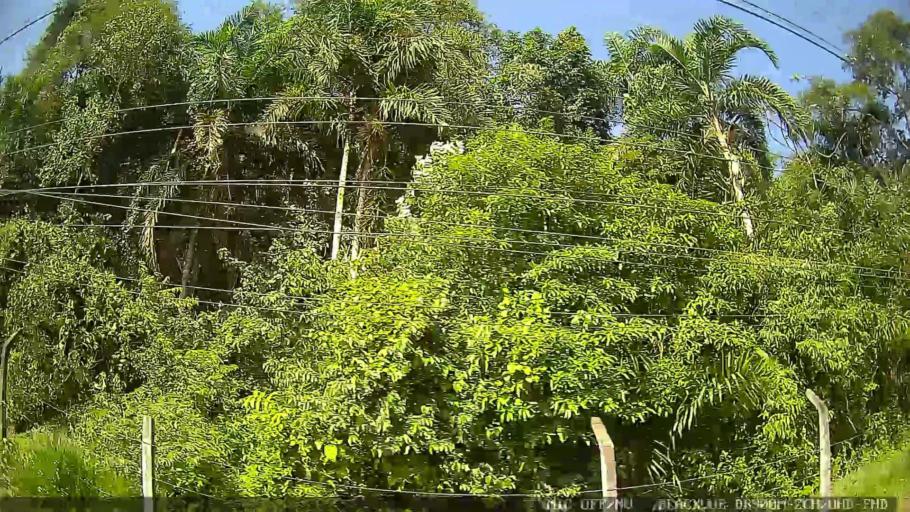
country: BR
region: Sao Paulo
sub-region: Guaruja
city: Guaruja
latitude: -24.0116
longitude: -46.2994
